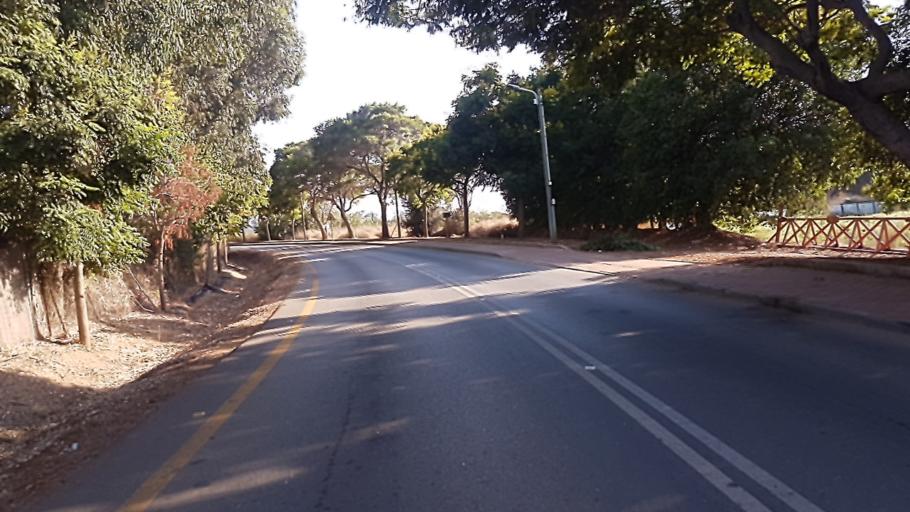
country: IL
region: Central District
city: Hod HaSharon
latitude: 32.1363
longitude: 34.9075
